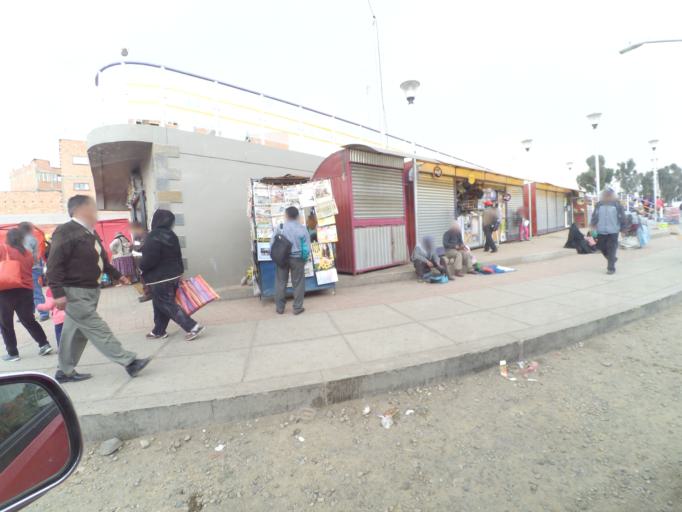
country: BO
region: La Paz
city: La Paz
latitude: -16.5037
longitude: -68.1612
